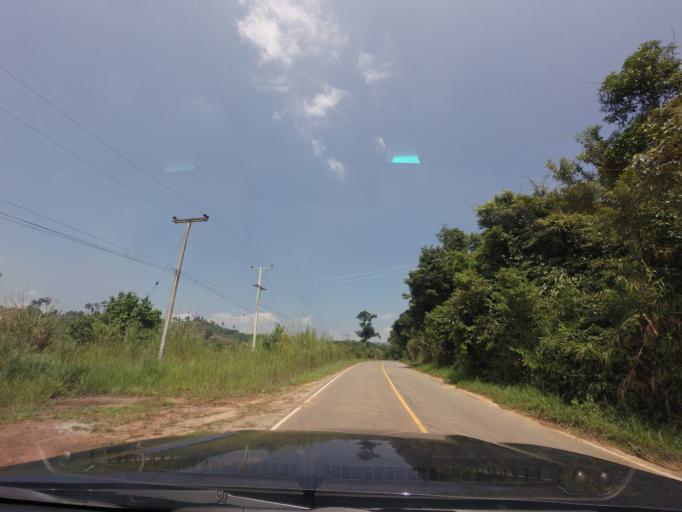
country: TH
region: Loei
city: Na Haeo
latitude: 17.5344
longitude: 100.8784
